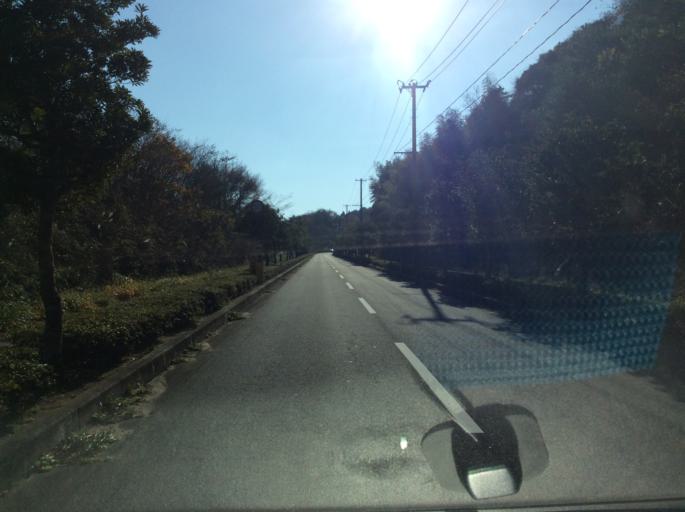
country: JP
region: Fukushima
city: Iwaki
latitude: 37.0228
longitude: 140.9249
